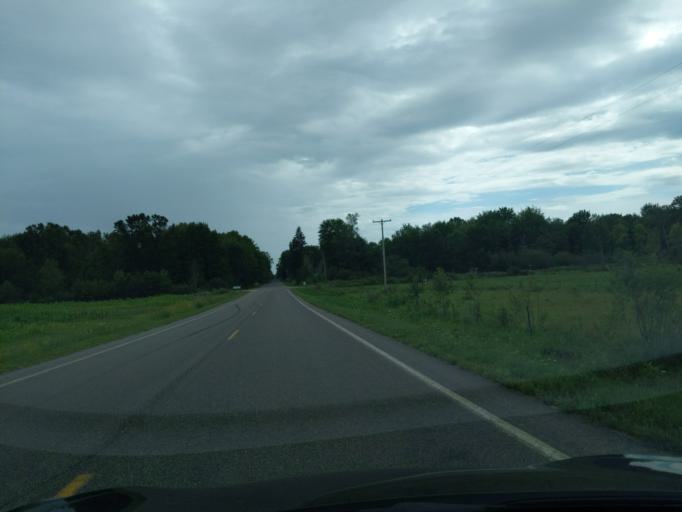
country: US
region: Michigan
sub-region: Clare County
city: Harrison
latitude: 44.0037
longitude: -84.9491
